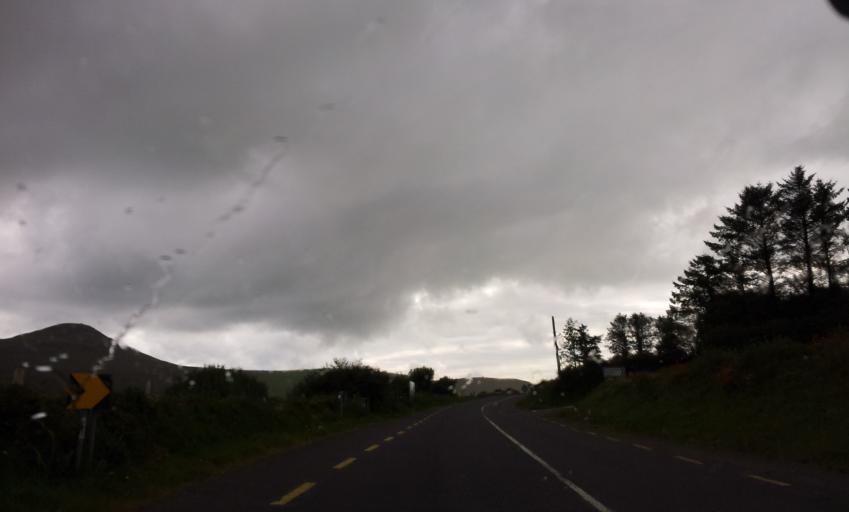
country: IE
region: Munster
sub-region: Ciarrai
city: Killorglin
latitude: 52.1753
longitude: -9.9892
